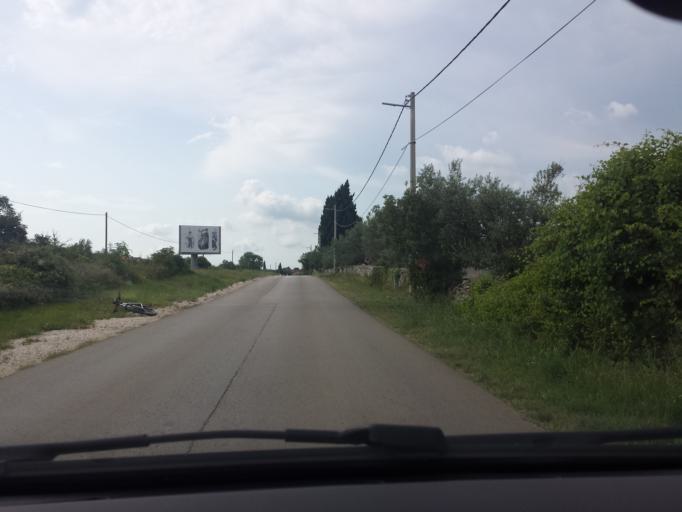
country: HR
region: Istarska
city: Galizana
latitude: 44.9386
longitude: 13.8684
